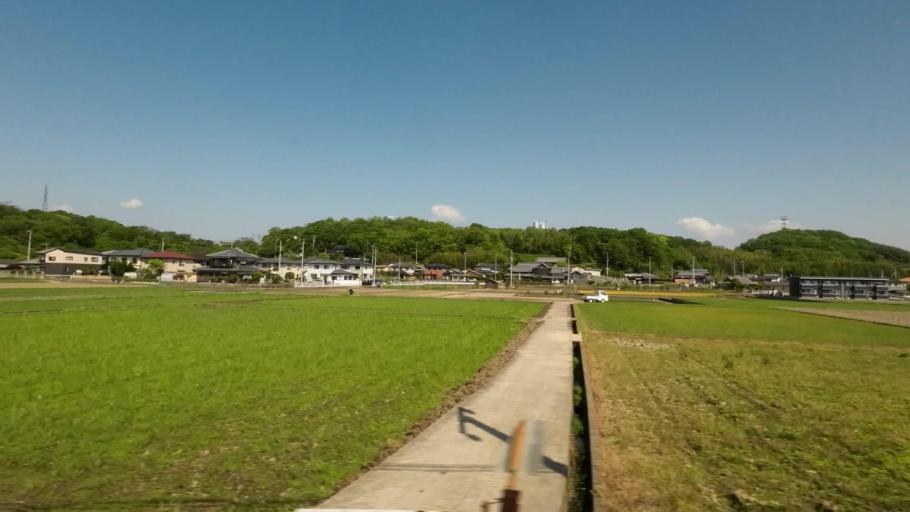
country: JP
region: Kagawa
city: Tadotsu
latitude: 34.2575
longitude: 133.7475
